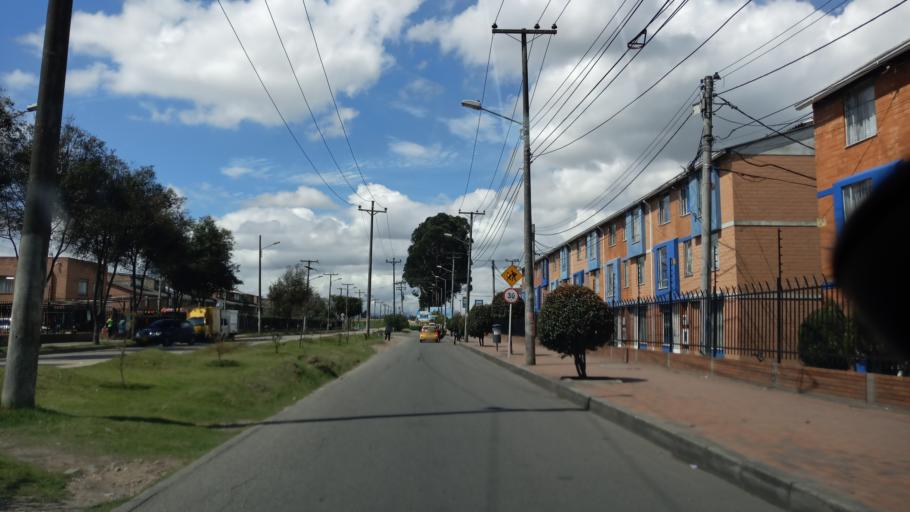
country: CO
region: Cundinamarca
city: Funza
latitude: 4.6698
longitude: -74.1573
